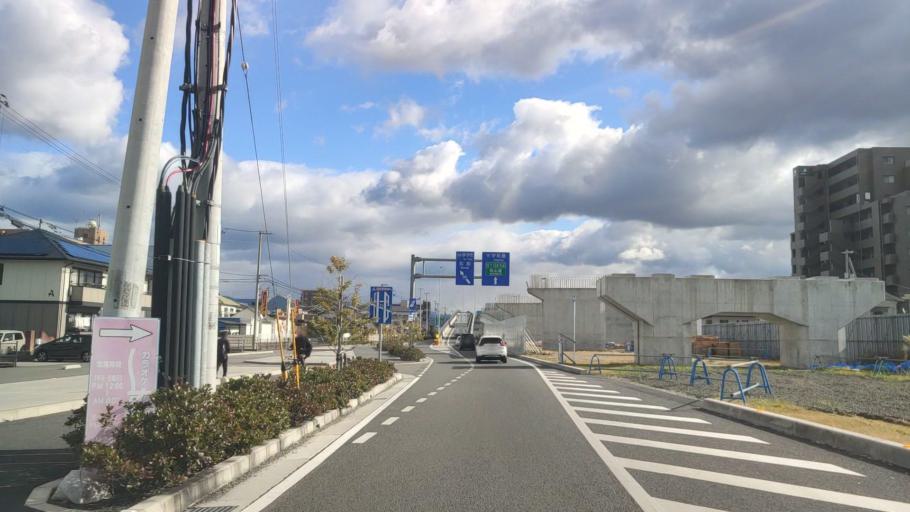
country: JP
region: Ehime
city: Masaki-cho
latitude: 33.8114
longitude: 132.7267
